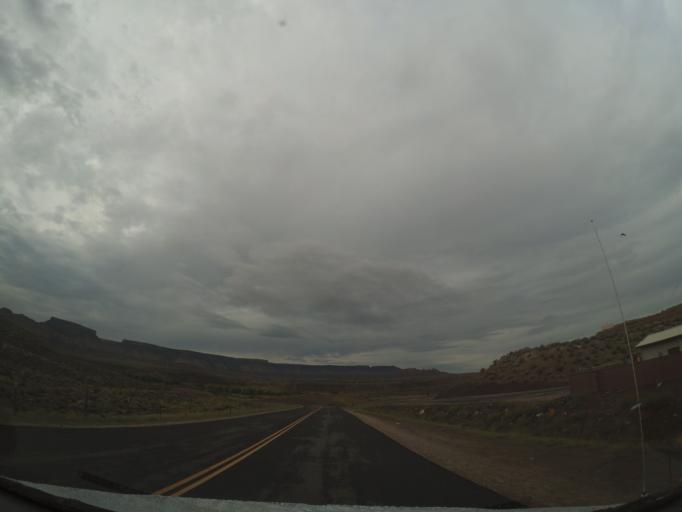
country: US
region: Utah
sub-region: Washington County
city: LaVerkin
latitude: 37.2072
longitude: -113.1747
